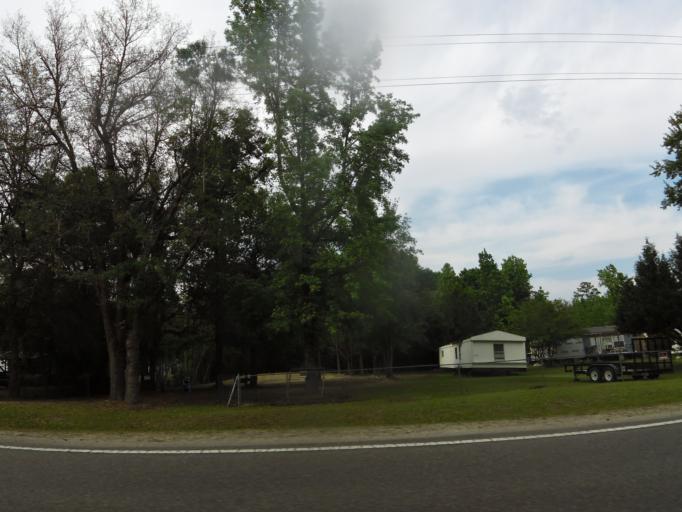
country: US
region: Florida
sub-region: Nassau County
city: Hilliard
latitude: 30.6984
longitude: -81.8908
